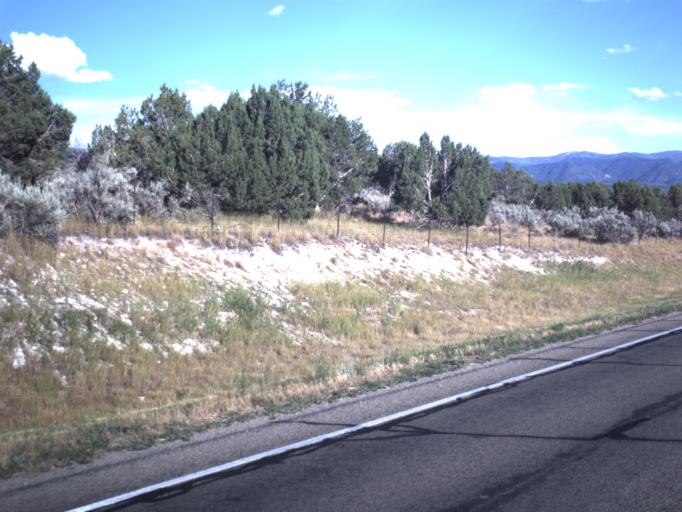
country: US
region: Utah
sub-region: Sanpete County
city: Fairview
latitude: 39.6433
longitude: -111.4496
